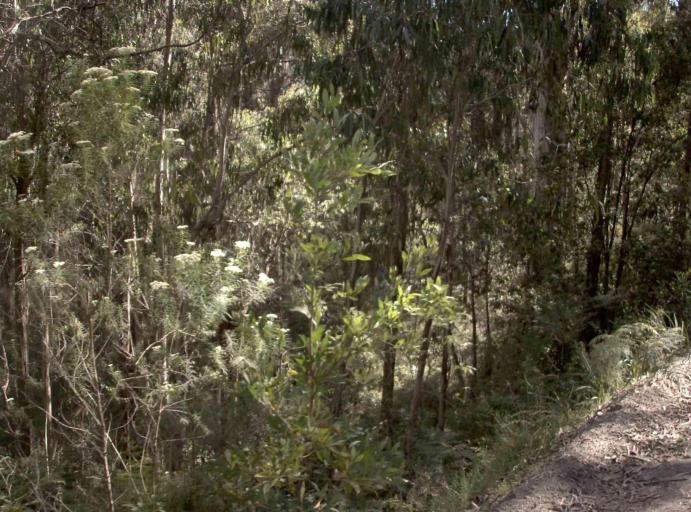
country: AU
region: New South Wales
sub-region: Bombala
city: Bombala
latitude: -37.2500
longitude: 148.7448
